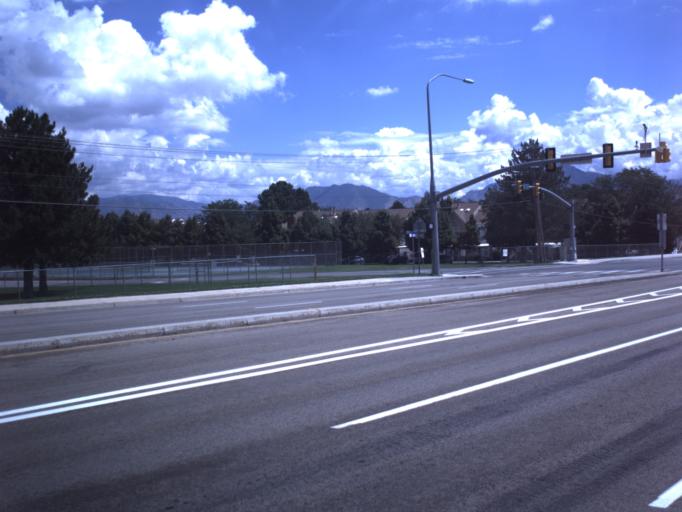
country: US
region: Utah
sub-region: Salt Lake County
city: Taylorsville
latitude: 40.6530
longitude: -111.9348
